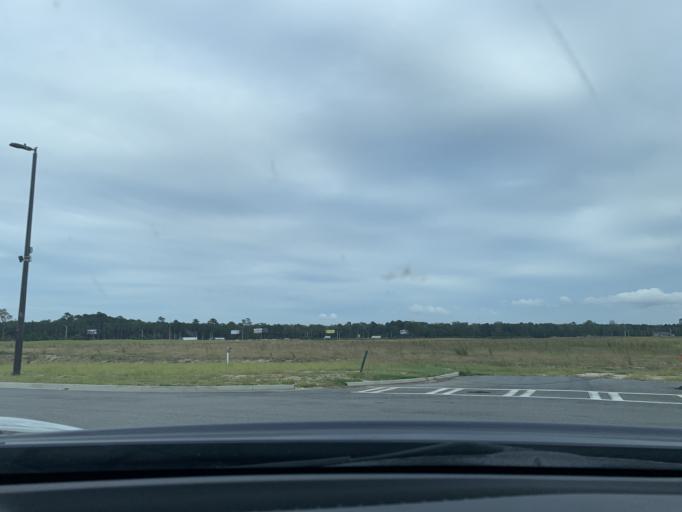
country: US
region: Georgia
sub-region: Chatham County
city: Pooler
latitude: 32.0798
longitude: -81.2803
